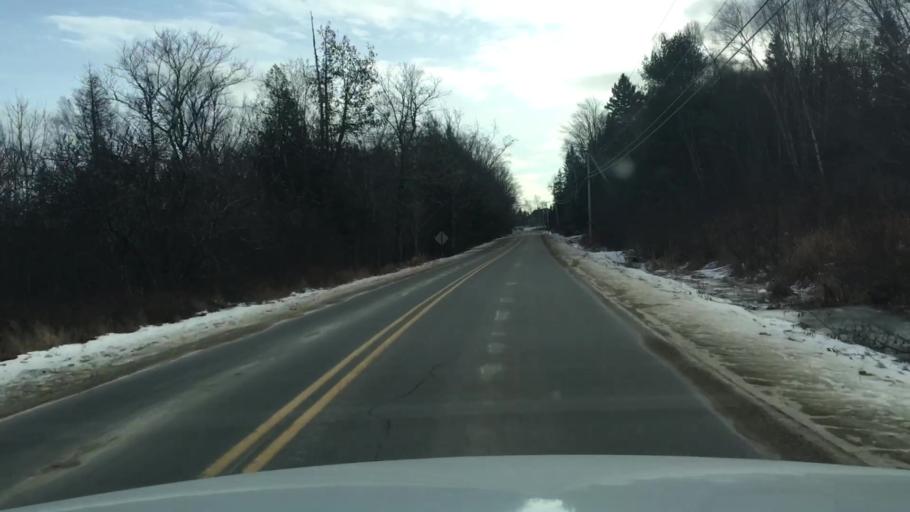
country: US
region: Maine
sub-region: Washington County
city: Jonesport
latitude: 44.6127
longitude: -67.6023
